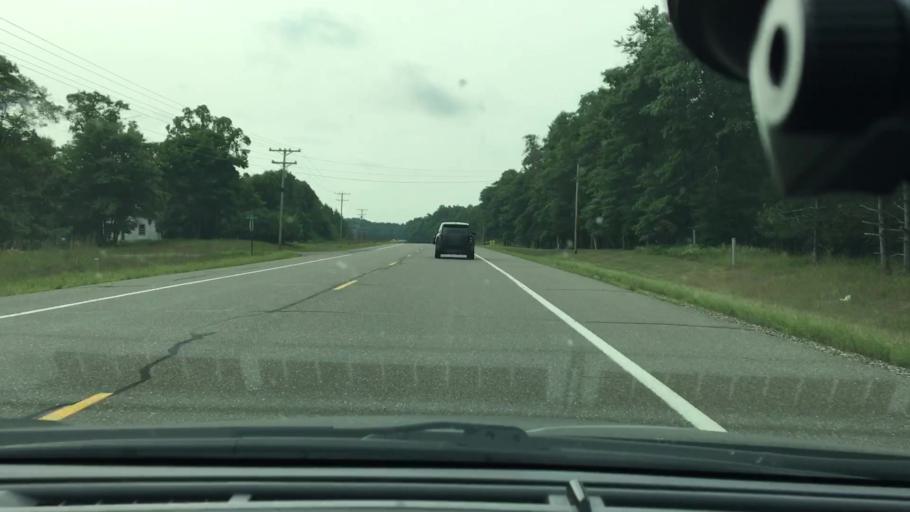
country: US
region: Minnesota
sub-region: Crow Wing County
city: Cross Lake
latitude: 46.6103
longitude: -94.1319
